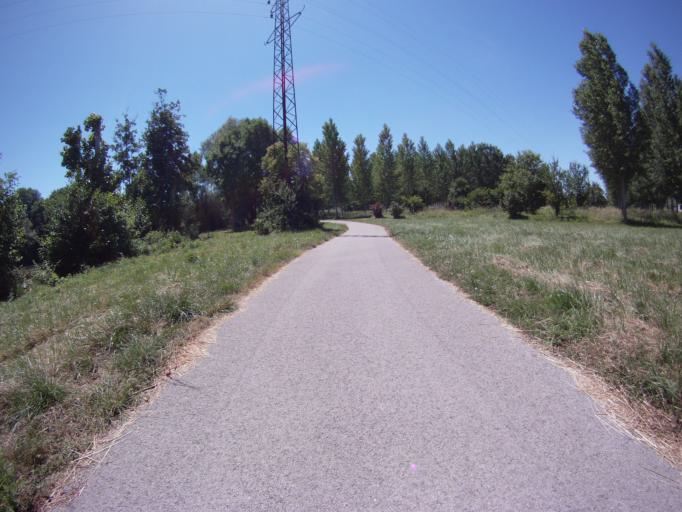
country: FR
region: Champagne-Ardenne
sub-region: Departement de la Marne
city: Mardeuil
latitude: 49.0666
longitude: 3.9201
